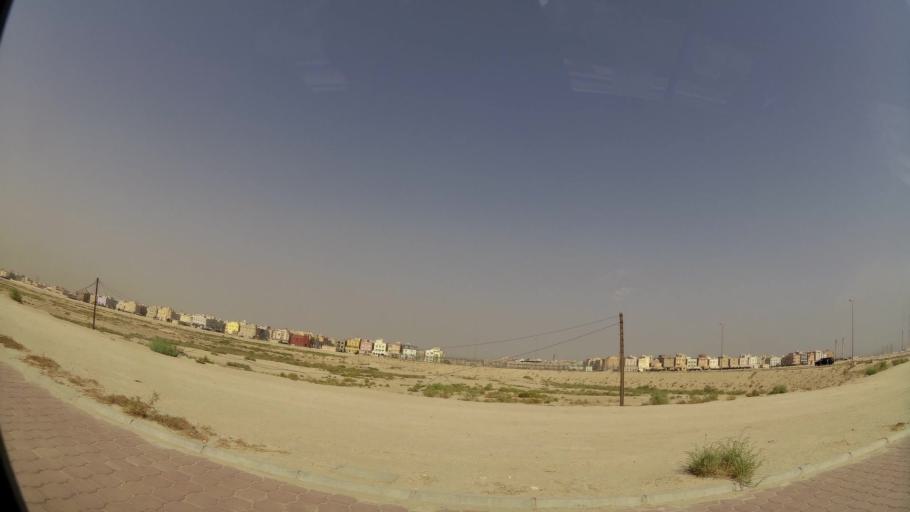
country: KW
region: Muhafazat al Jahra'
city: Al Jahra'
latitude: 29.3327
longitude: 47.7736
